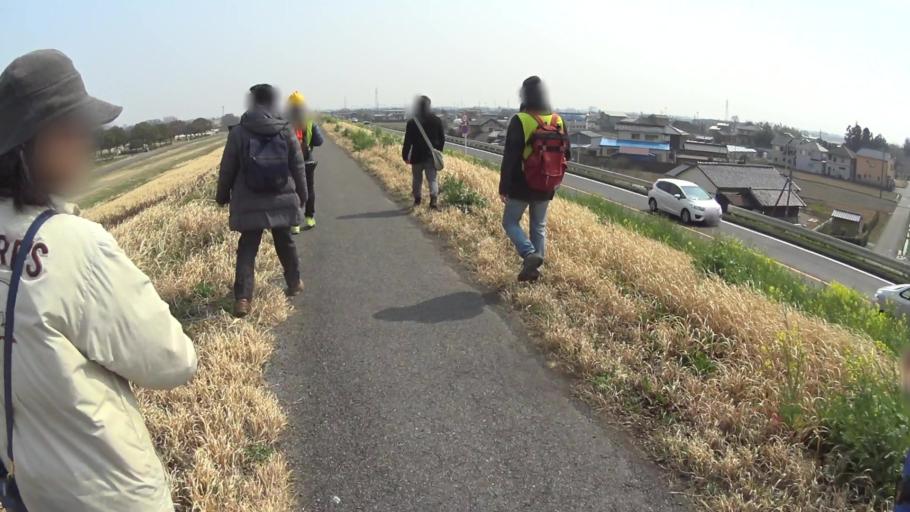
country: JP
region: Tochigi
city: Fujioka
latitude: 36.2053
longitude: 139.6700
